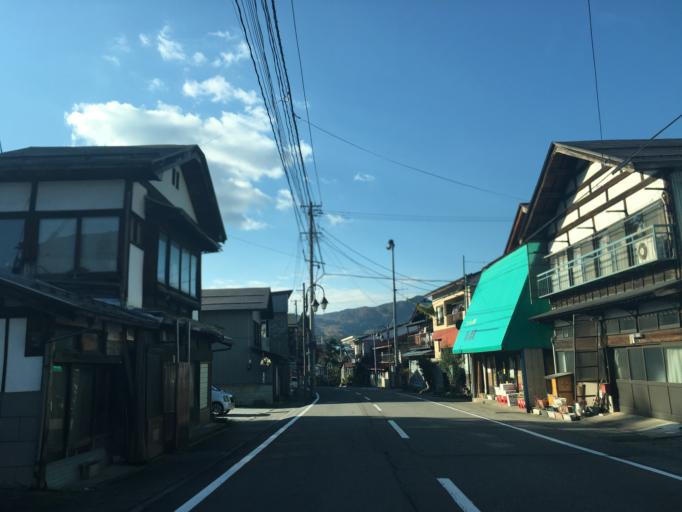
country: JP
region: Fukushima
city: Kitakata
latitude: 37.5871
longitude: 139.6437
